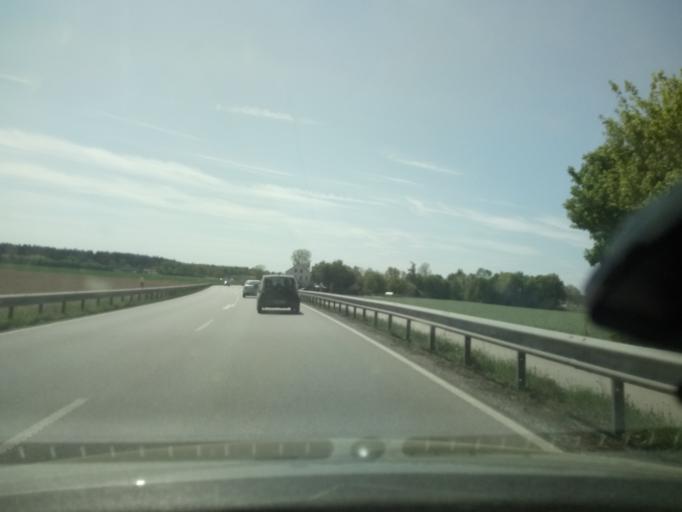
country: DE
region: Bavaria
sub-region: Upper Bavaria
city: Ampfing
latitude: 48.2419
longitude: 12.4123
